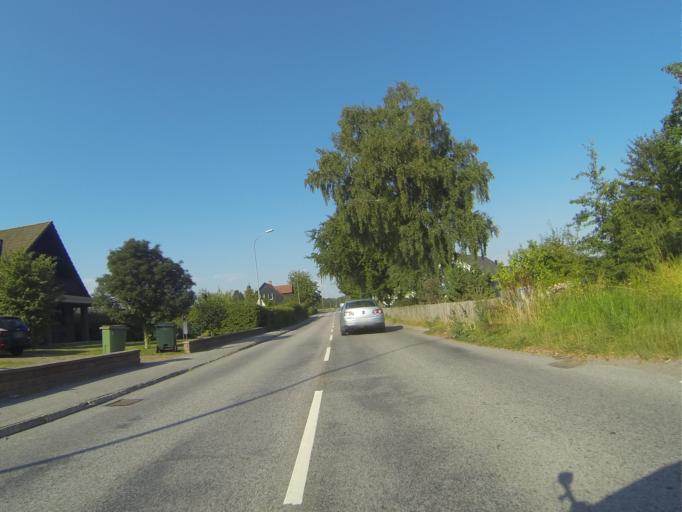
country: SE
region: Skane
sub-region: Svedala Kommun
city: Klagerup
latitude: 55.5801
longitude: 13.1951
